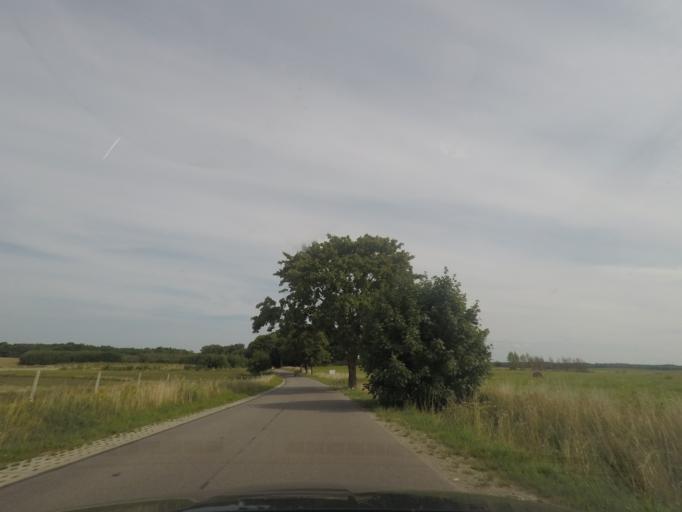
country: PL
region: Pomeranian Voivodeship
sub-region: Slupsk
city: Slupsk
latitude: 54.6011
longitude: 17.0519
